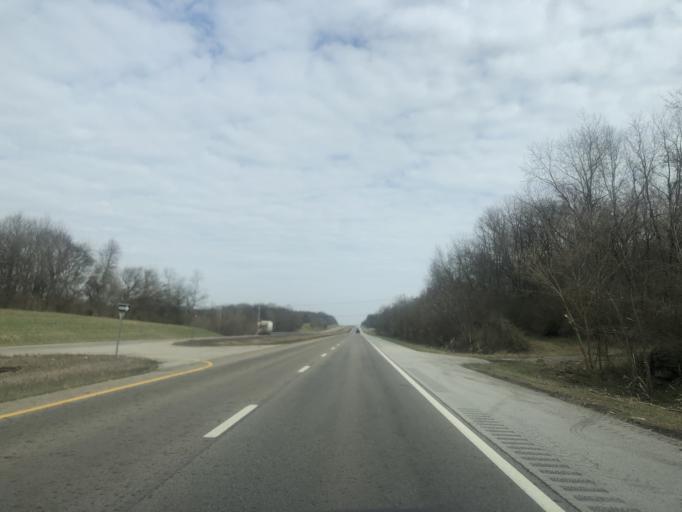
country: US
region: Tennessee
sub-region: Maury County
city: Mount Pleasant
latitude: 35.5714
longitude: -87.1605
